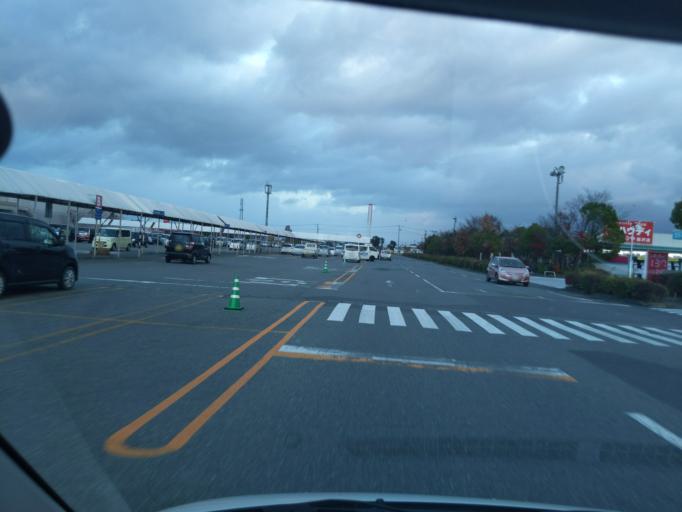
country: JP
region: Iwate
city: Mizusawa
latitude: 39.0516
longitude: 141.1306
